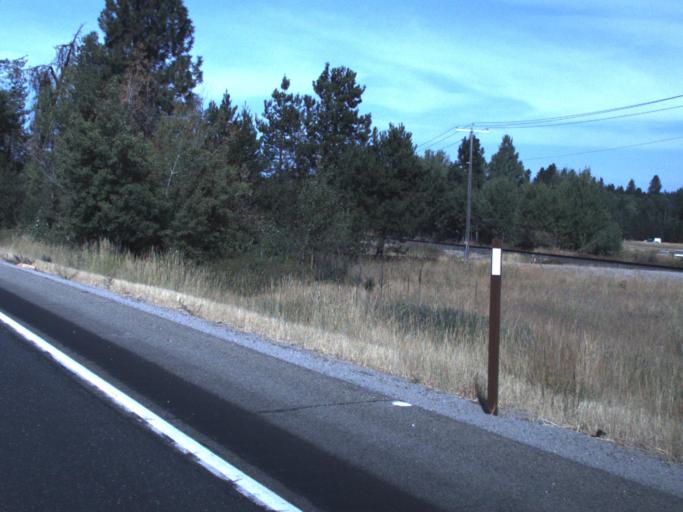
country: US
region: Washington
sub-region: Spokane County
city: Deer Park
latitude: 47.9931
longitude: -117.5458
